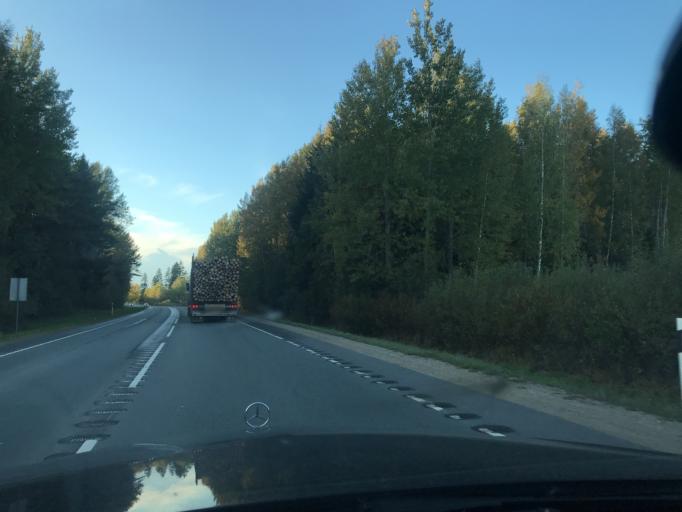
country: EE
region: Vorumaa
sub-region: Voru linn
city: Voru
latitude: 57.8628
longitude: 26.9656
